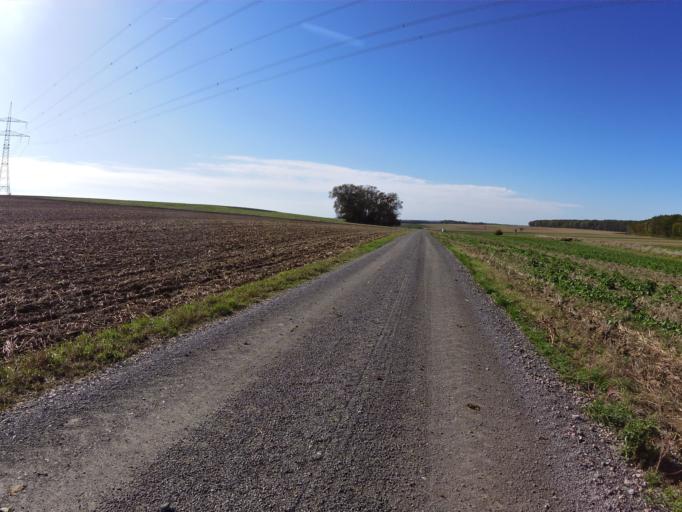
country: DE
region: Bavaria
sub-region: Regierungsbezirk Unterfranken
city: Theilheim
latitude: 49.7418
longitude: 10.0526
